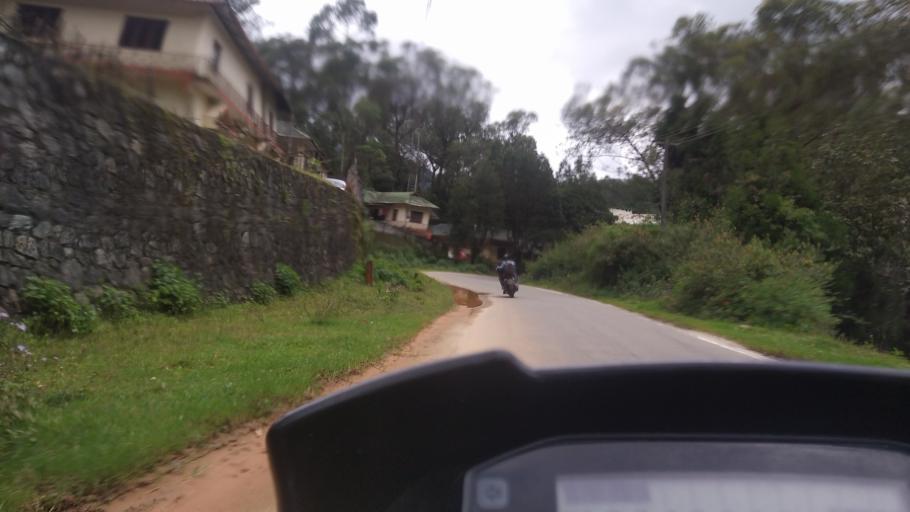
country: IN
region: Kerala
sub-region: Idukki
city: Munnar
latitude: 10.0699
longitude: 77.0990
